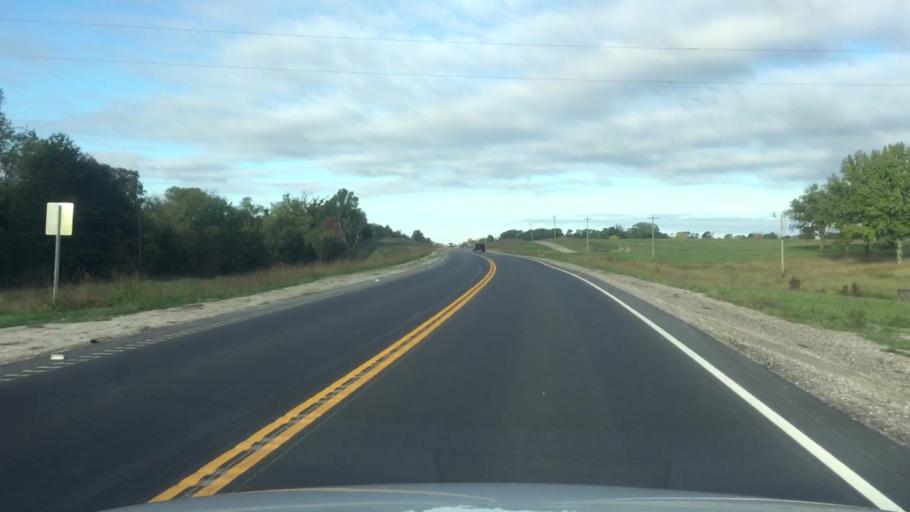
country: US
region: Missouri
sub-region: Boone County
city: Columbia
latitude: 38.9886
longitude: -92.4665
